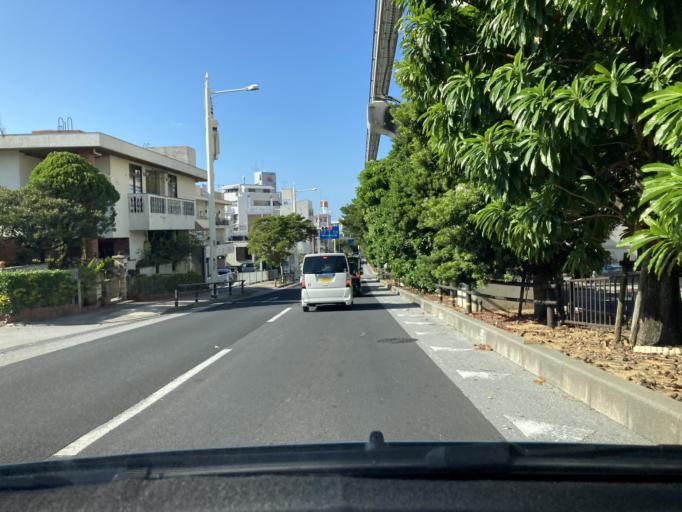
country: JP
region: Okinawa
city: Naha-shi
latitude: 26.2223
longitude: 127.7211
